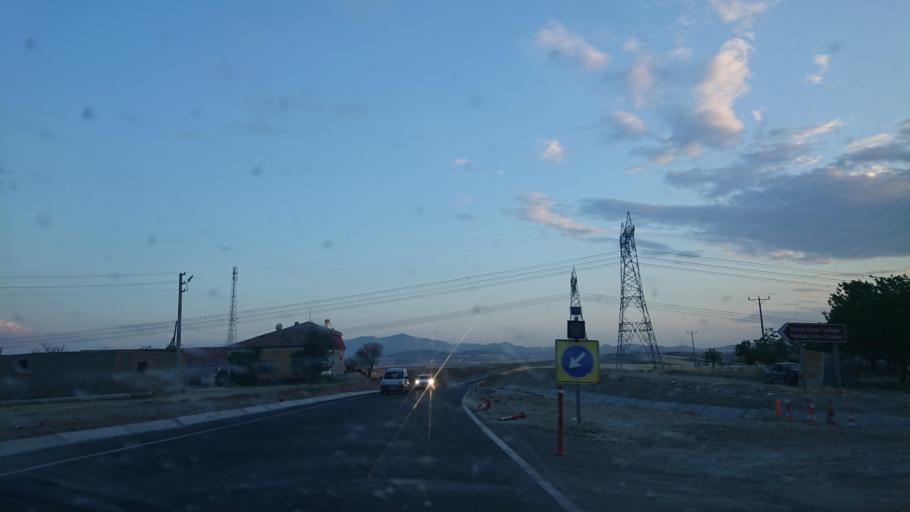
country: TR
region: Aksaray
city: Balci
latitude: 38.7858
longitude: 34.1195
